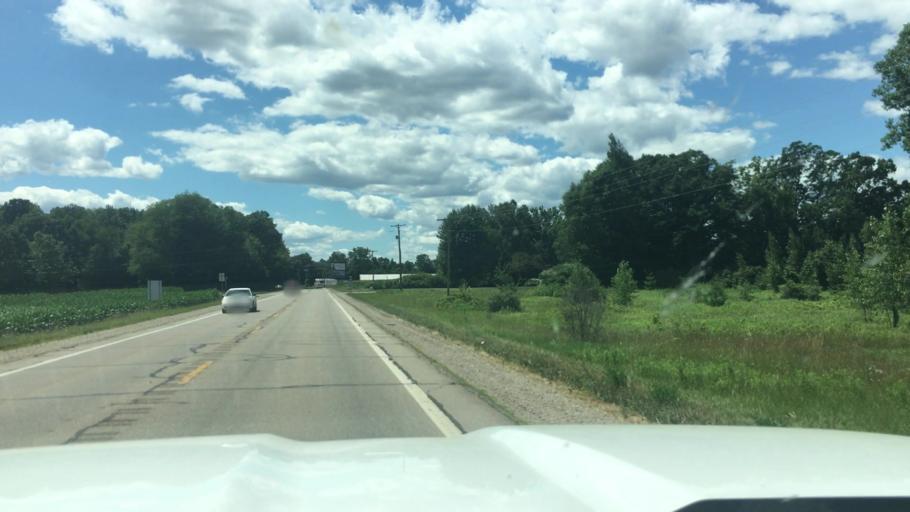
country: US
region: Michigan
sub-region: Montcalm County
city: Greenville
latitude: 43.1706
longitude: -85.1510
